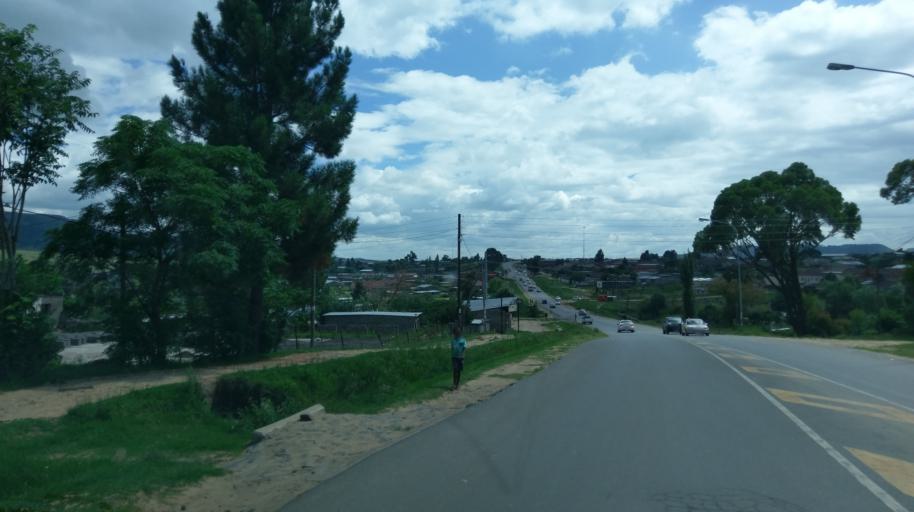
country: LS
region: Maseru
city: Maseru
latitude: -29.2832
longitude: 27.5276
